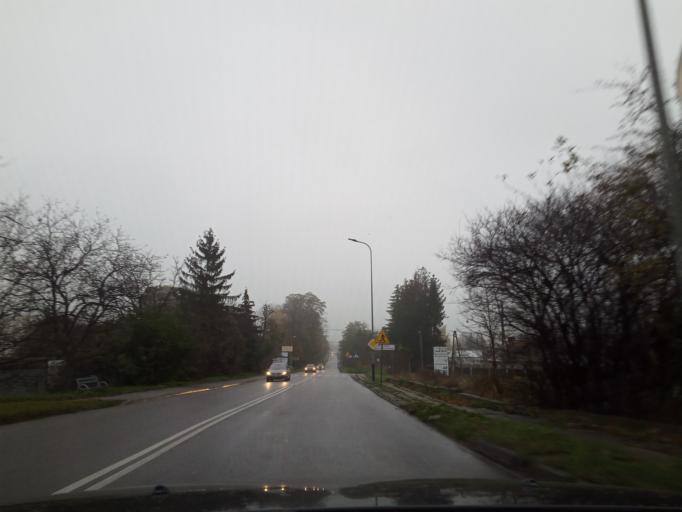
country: PL
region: Lesser Poland Voivodeship
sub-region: Powiat wielicki
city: Kokotow
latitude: 50.0984
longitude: 20.0662
